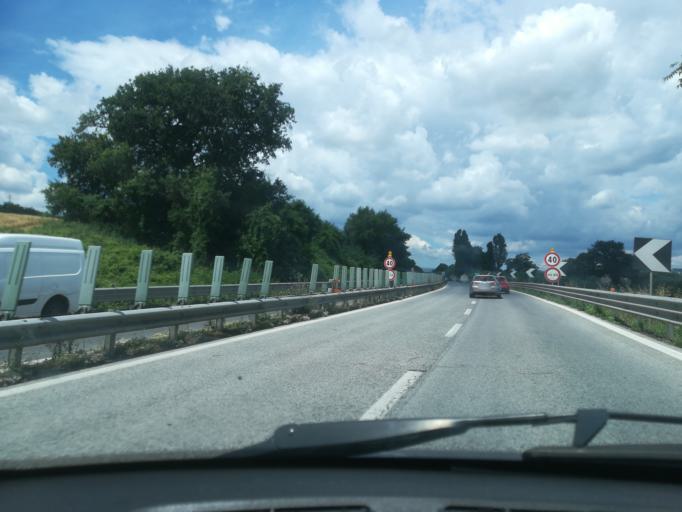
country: IT
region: The Marches
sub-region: Provincia di Macerata
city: Corridonia
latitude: 43.2683
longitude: 13.5204
